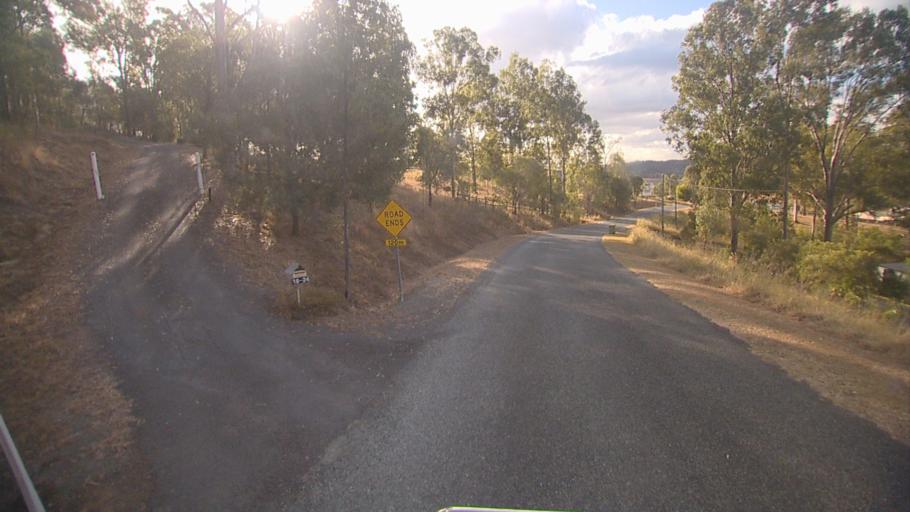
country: AU
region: Queensland
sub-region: Logan
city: Cedar Vale
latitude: -27.8990
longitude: 153.0718
